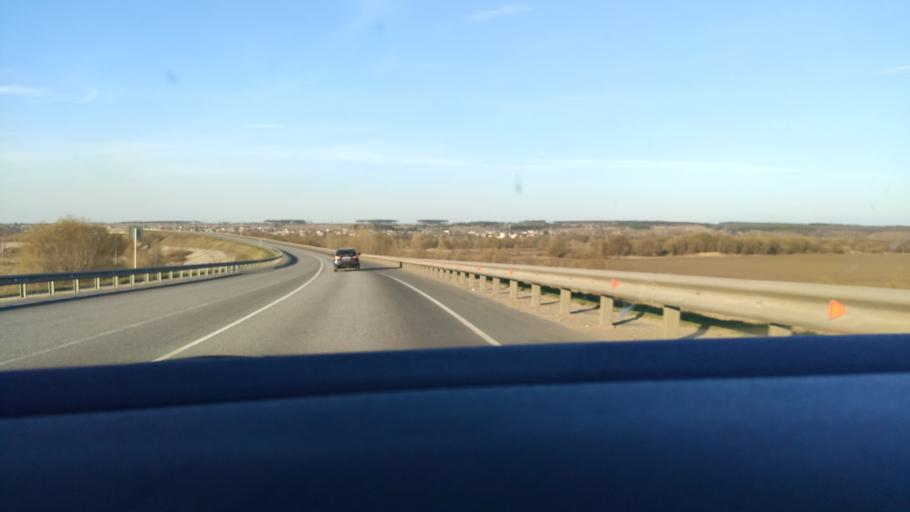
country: RU
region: Voronezj
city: Kolodeznyy
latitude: 51.3304
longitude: 39.1615
